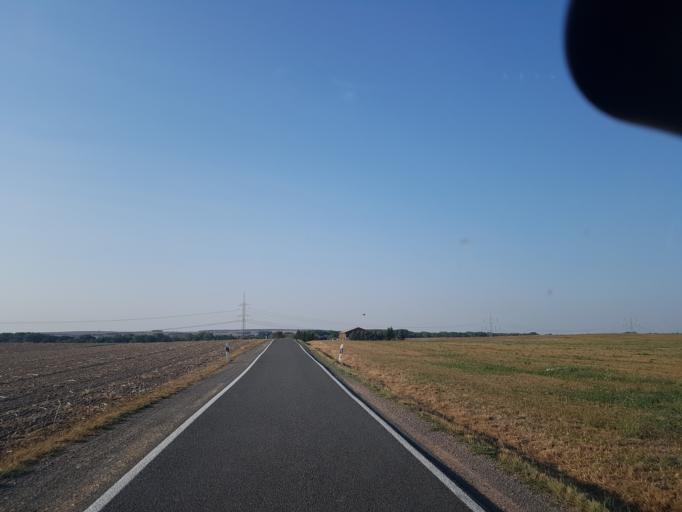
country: DE
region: Saxony
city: Stauchitz
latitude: 51.2959
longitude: 13.1909
